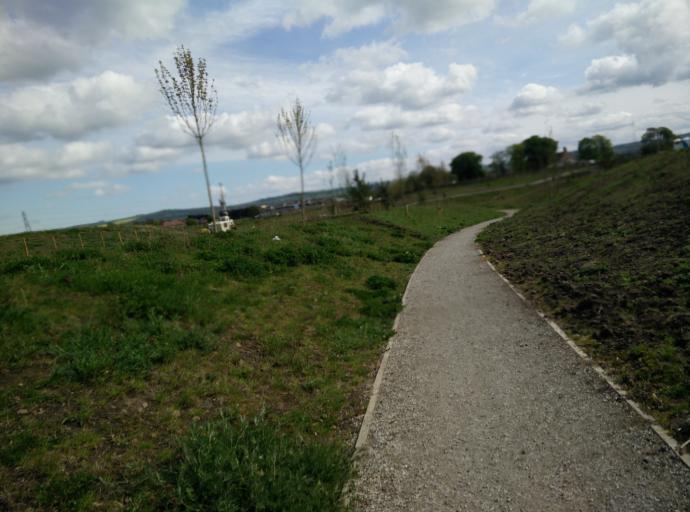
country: GB
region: Scotland
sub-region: Midlothian
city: Dalkeith
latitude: 55.9137
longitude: -3.1015
